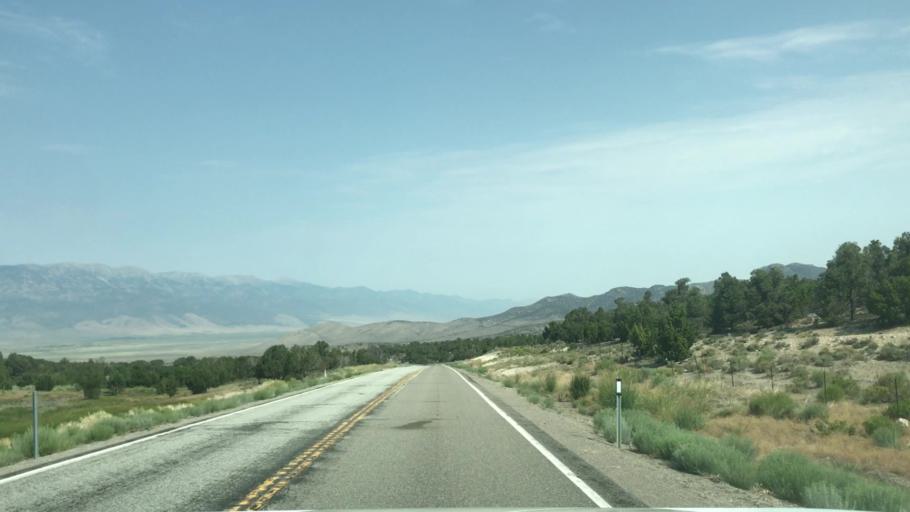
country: US
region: Nevada
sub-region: White Pine County
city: McGill
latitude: 39.1536
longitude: -114.3472
